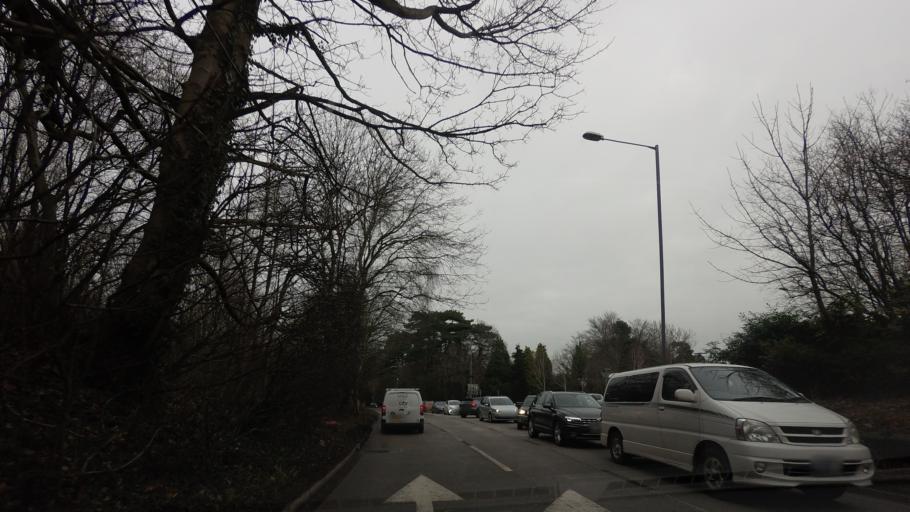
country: GB
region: England
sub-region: East Sussex
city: Saint Leonards-on-Sea
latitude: 50.8920
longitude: 0.5559
